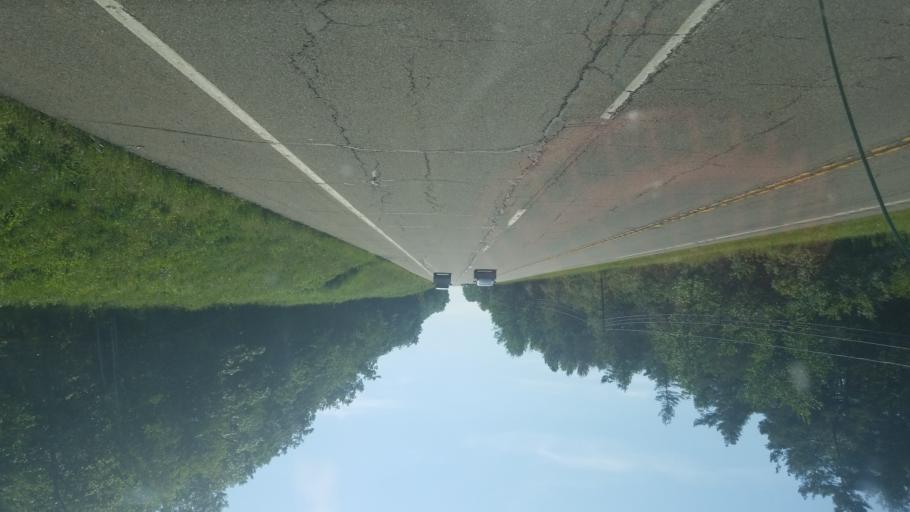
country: US
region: New York
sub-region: Allegany County
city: Wellsville
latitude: 42.1169
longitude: -78.0082
